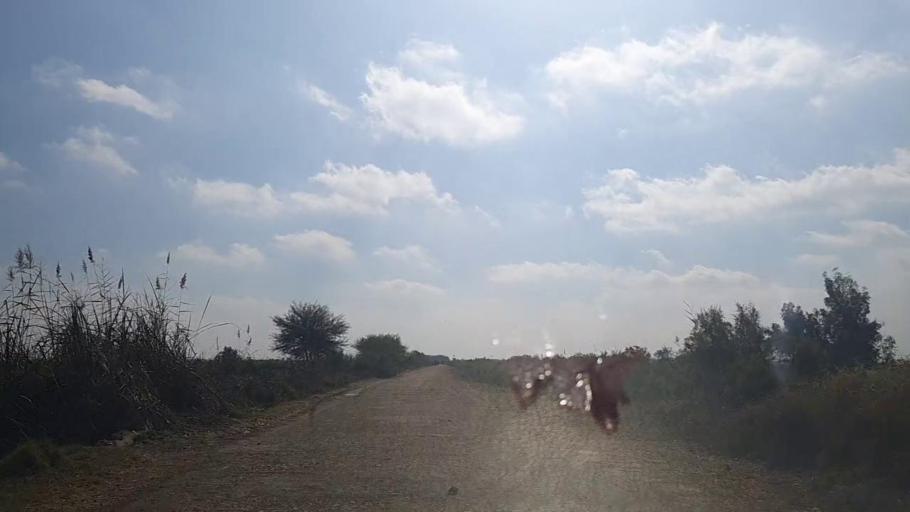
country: PK
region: Sindh
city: Sanghar
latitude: 26.0607
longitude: 69.0055
